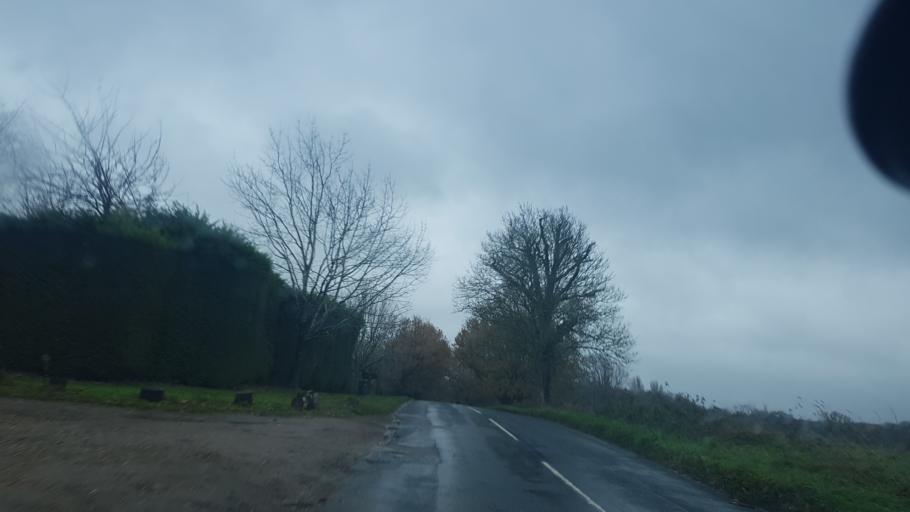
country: GB
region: England
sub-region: Surrey
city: Ripley
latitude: 51.2785
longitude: -0.5004
